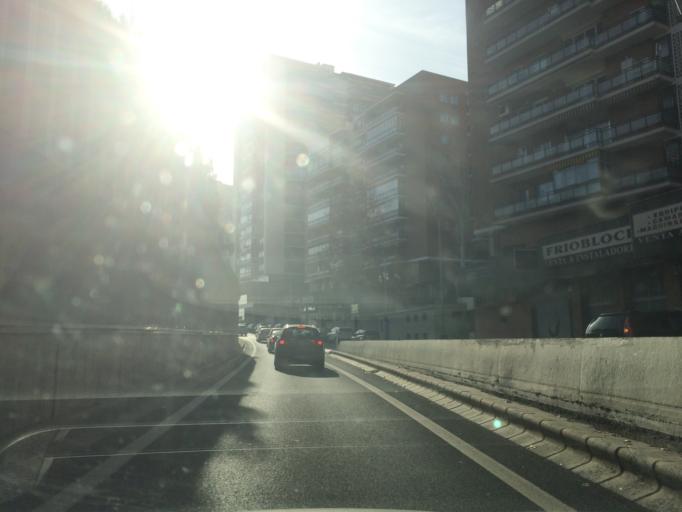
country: ES
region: Madrid
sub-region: Provincia de Madrid
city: City Center
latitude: 40.4157
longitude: -3.7237
